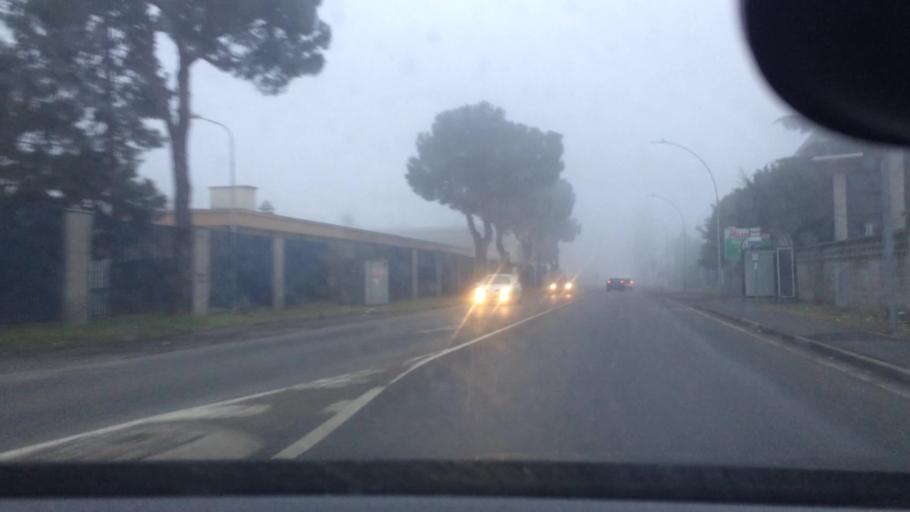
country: IT
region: Lombardy
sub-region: Citta metropolitana di Milano
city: Lainate
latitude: 45.5776
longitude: 9.0161
